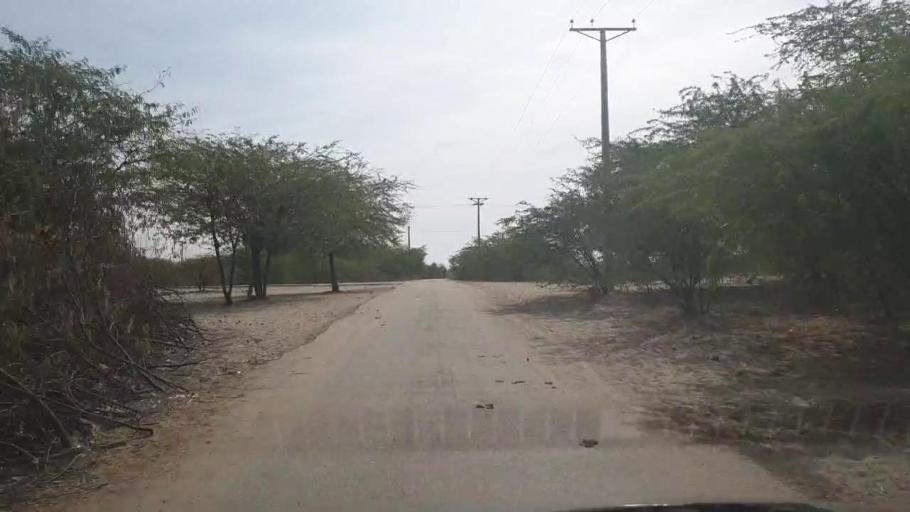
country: PK
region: Sindh
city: Umarkot
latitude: 25.2944
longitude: 69.7371
